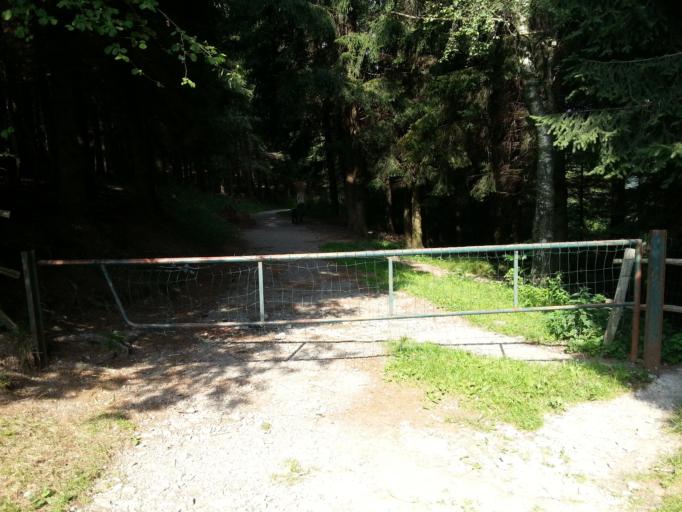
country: IT
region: Lombardy
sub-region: Provincia di Como
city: Caglio
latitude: 45.8827
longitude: 9.2279
